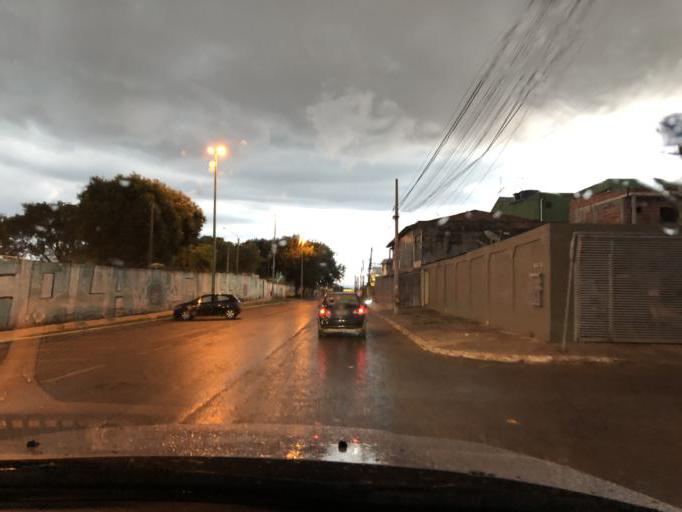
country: BR
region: Federal District
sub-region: Brasilia
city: Brasilia
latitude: -15.8074
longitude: -48.1171
